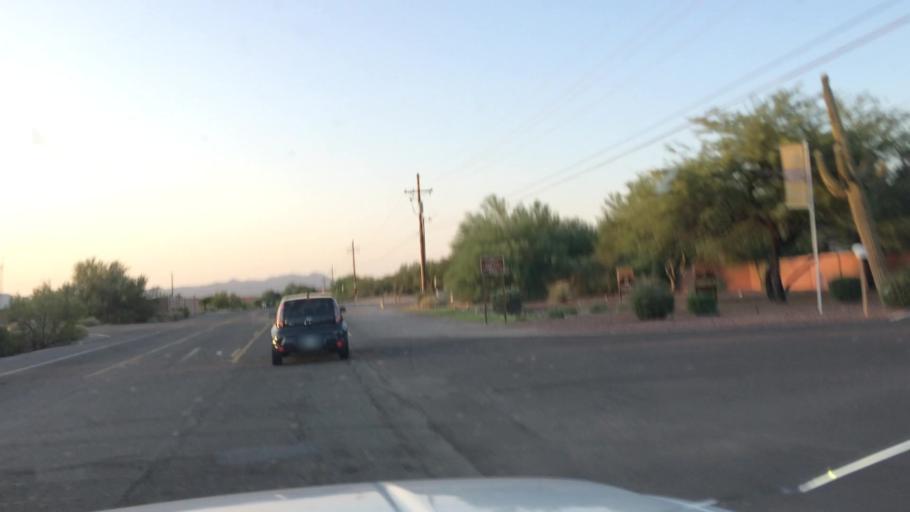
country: US
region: Arizona
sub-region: Pima County
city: Casas Adobes
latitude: 32.3433
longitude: -111.0204
